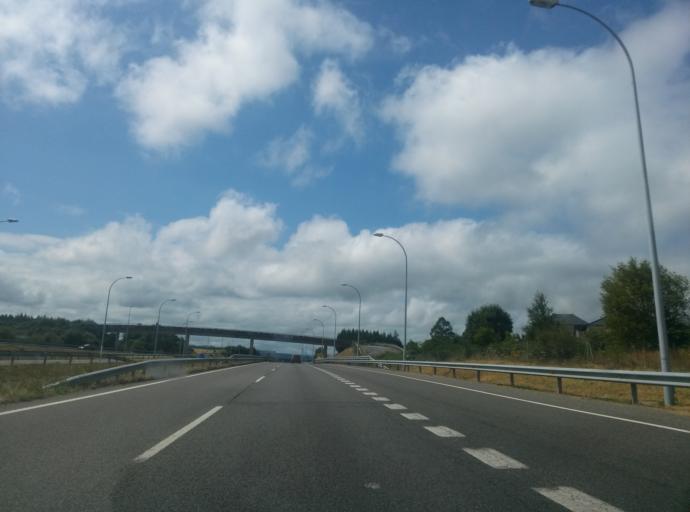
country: ES
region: Galicia
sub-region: Provincia de Lugo
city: Lugo
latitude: 43.0588
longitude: -7.5607
